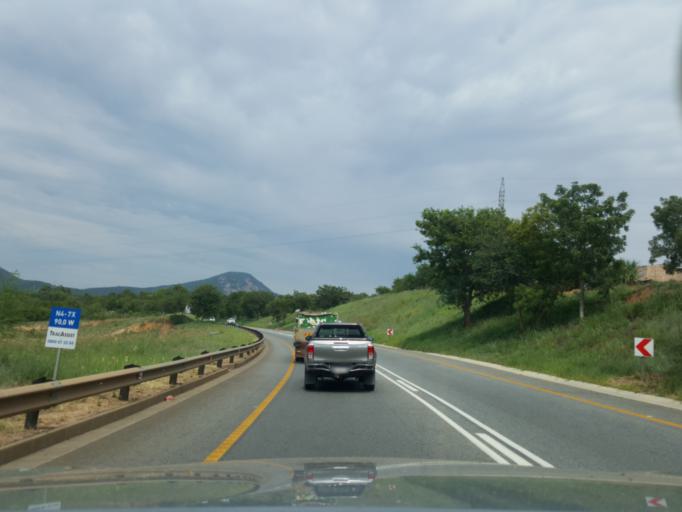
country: SZ
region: Hhohho
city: Ntfonjeni
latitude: -25.5361
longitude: 31.3099
